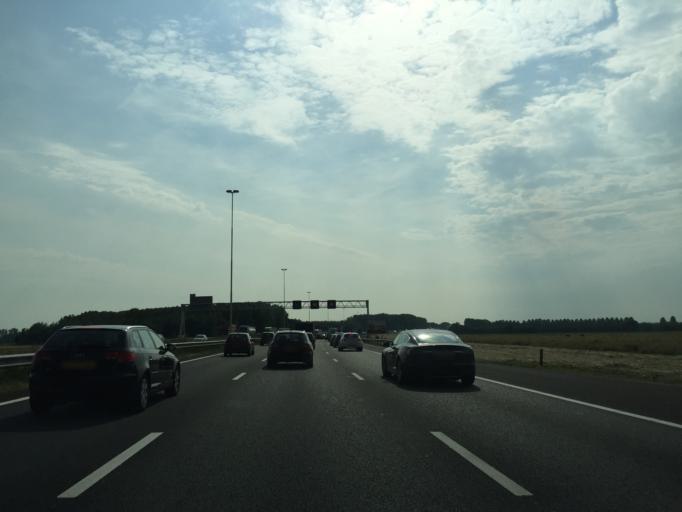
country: NL
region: Utrecht
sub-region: Gemeente Vianen
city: Vianen
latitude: 51.9569
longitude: 5.0730
